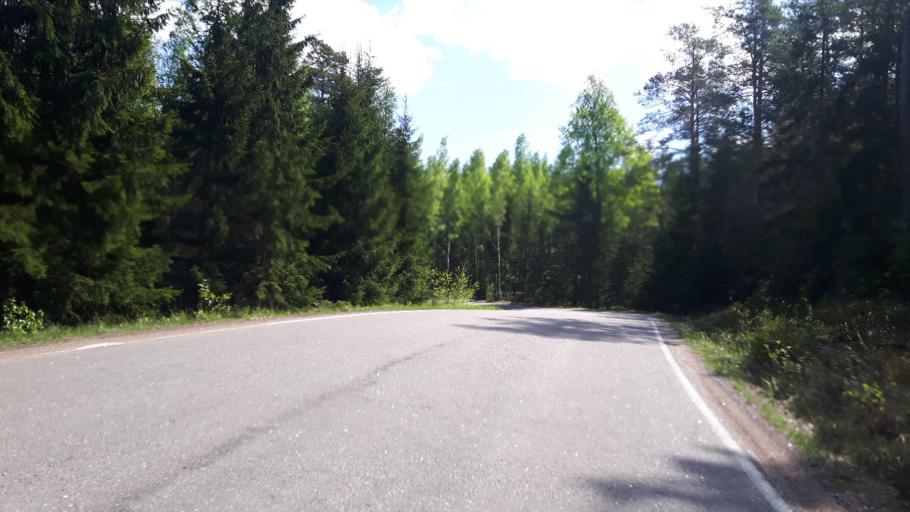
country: FI
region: Kymenlaakso
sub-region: Kotka-Hamina
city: Hamina
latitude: 60.5115
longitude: 27.4002
